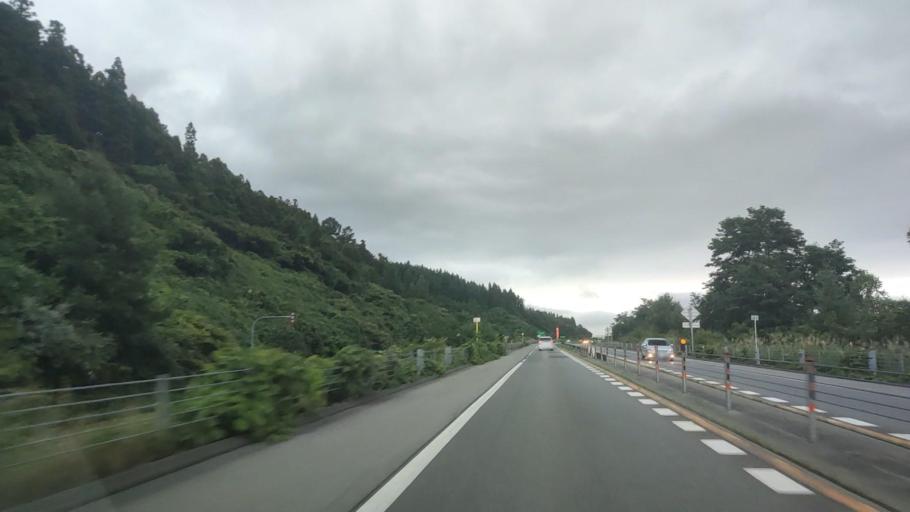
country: JP
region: Hokkaido
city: Nanae
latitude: 41.9100
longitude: 140.6941
